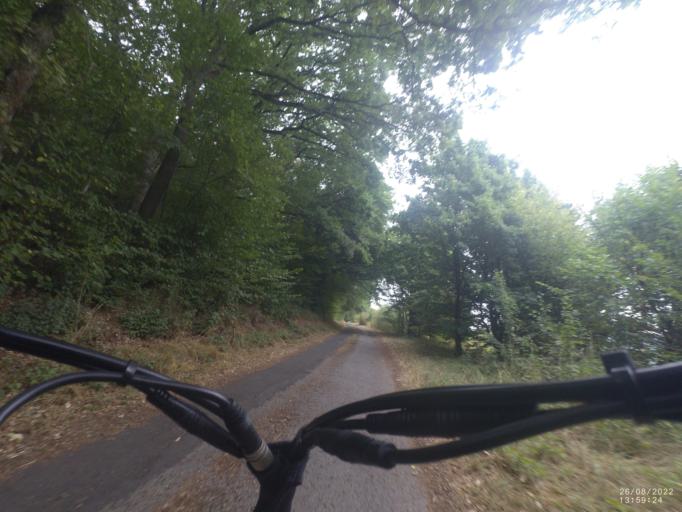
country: DE
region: Rheinland-Pfalz
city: Kalenborn-Scheuern
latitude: 50.2320
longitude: 6.6249
